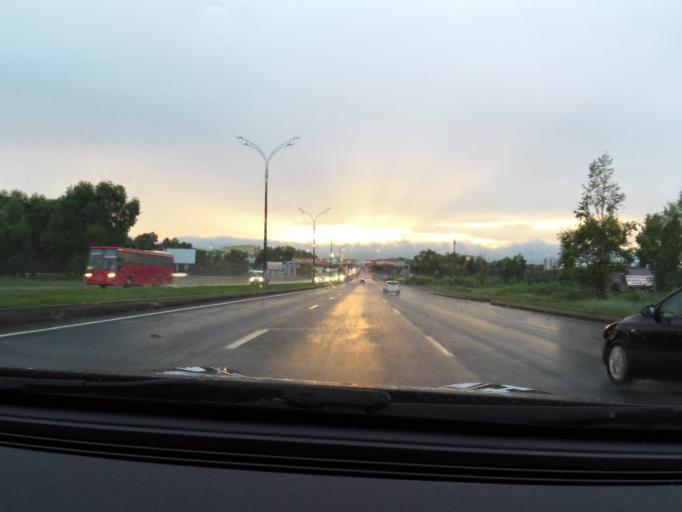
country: RU
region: Tatarstan
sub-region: Tukayevskiy Rayon
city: Naberezhnyye Chelny
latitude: 55.6687
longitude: 52.3002
